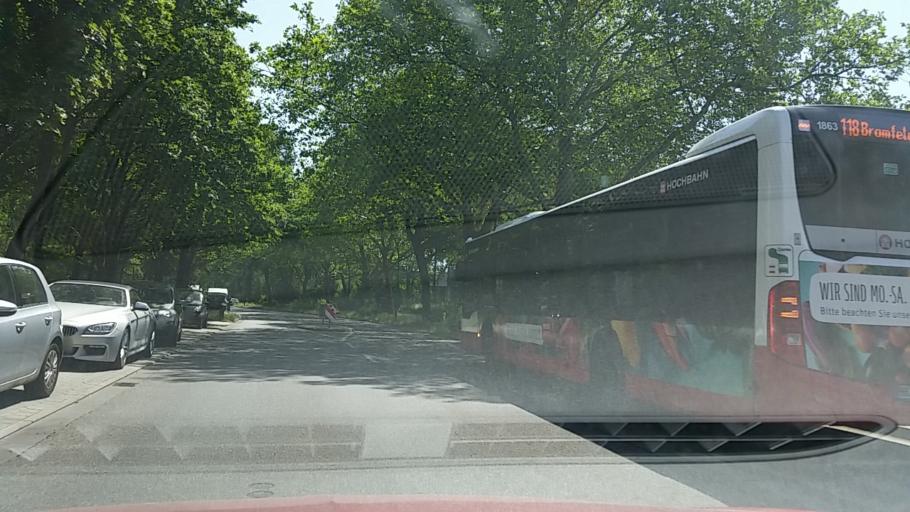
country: DE
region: Hamburg
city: Barmbek-Nord
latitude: 53.6113
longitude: 10.0464
